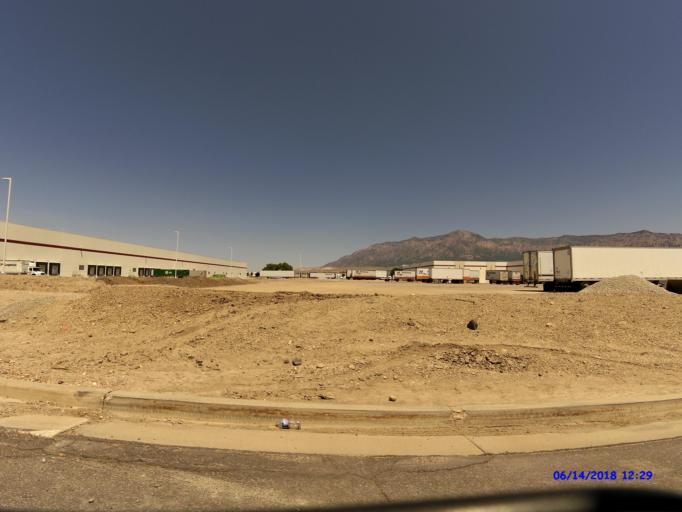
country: US
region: Utah
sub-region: Weber County
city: Harrisville
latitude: 41.2631
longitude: -112.0017
